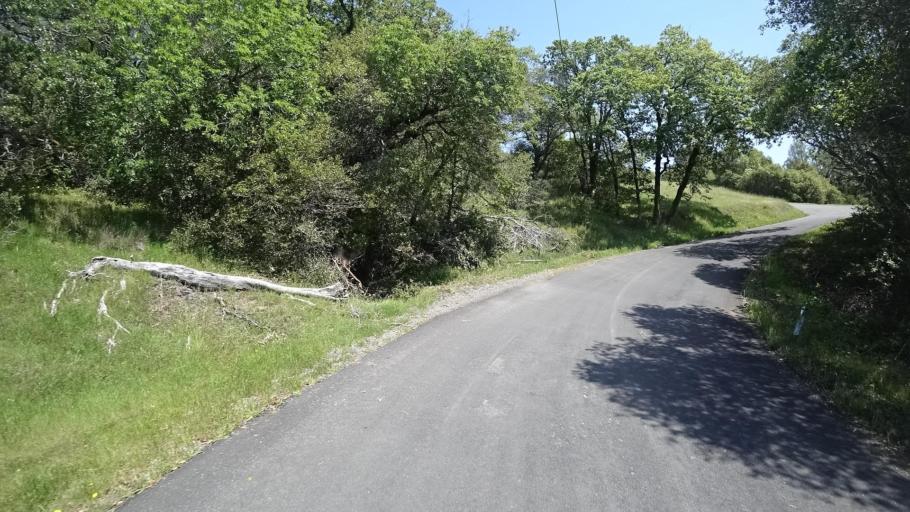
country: US
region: California
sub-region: Humboldt County
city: Redway
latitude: 40.2375
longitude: -123.6319
